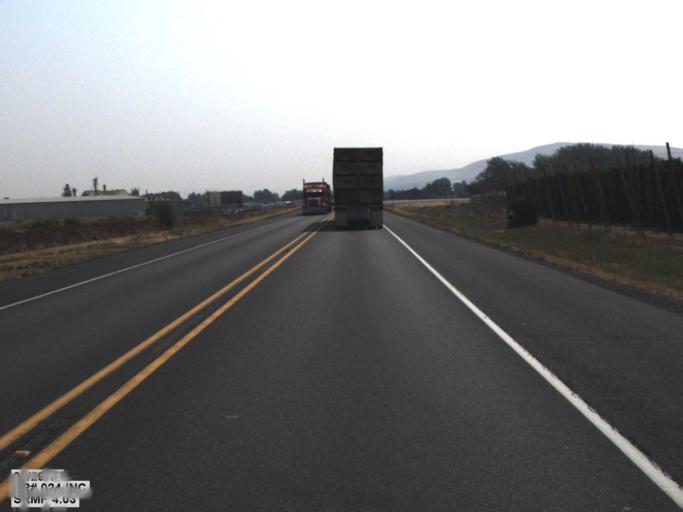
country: US
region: Washington
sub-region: Yakima County
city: Terrace Heights
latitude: 46.5607
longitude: -120.3998
